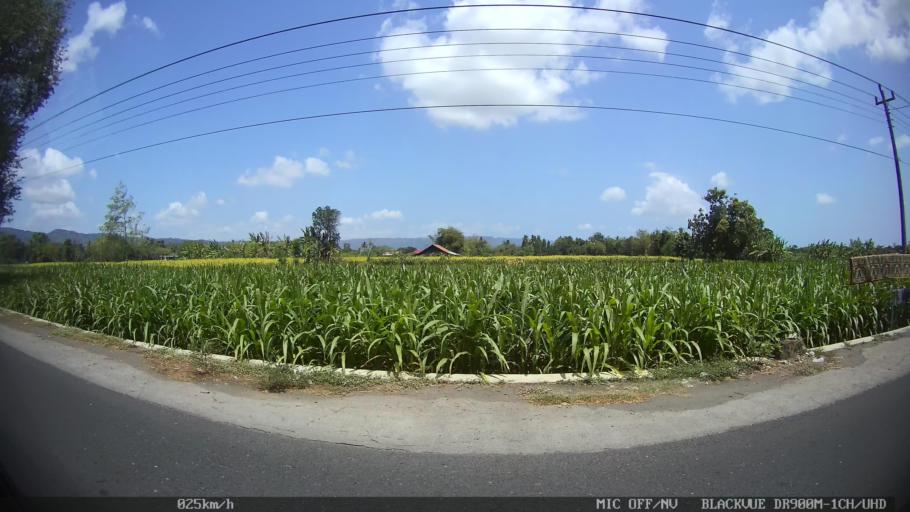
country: ID
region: Daerah Istimewa Yogyakarta
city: Sewon
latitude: -7.8977
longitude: 110.3767
